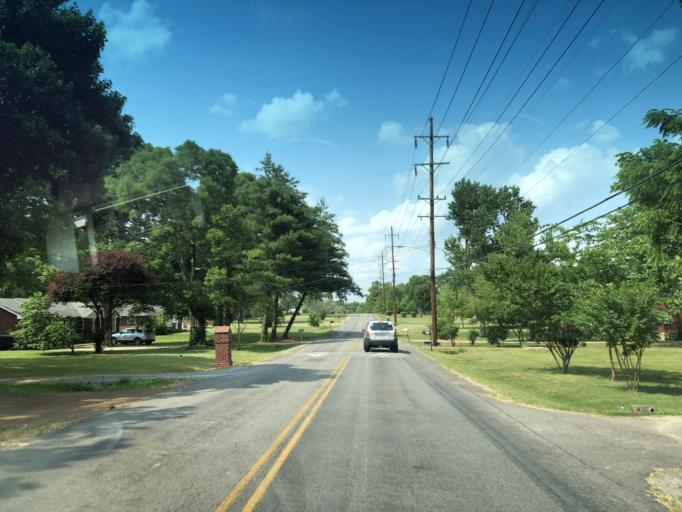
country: US
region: Tennessee
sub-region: Davidson County
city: Goodlettsville
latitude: 36.2577
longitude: -86.7195
